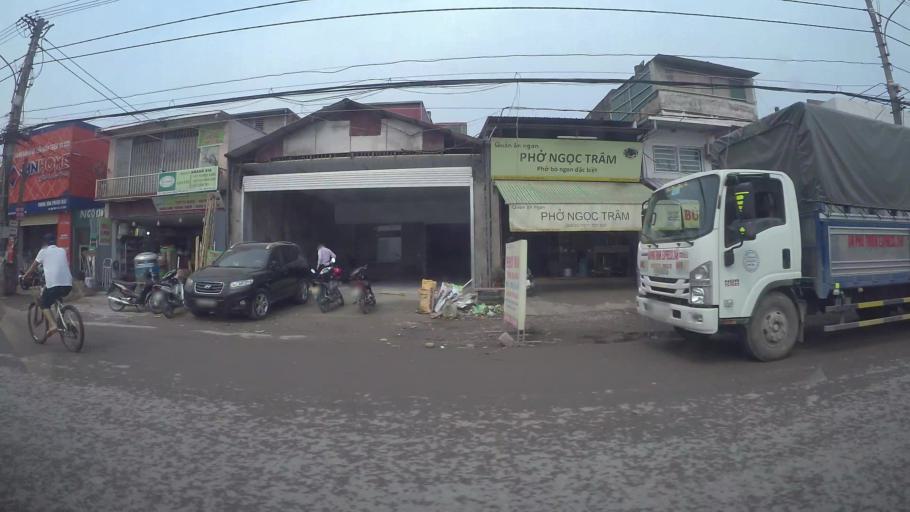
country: VN
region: Ha Noi
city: Van Dien
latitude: 20.9690
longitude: 105.8672
